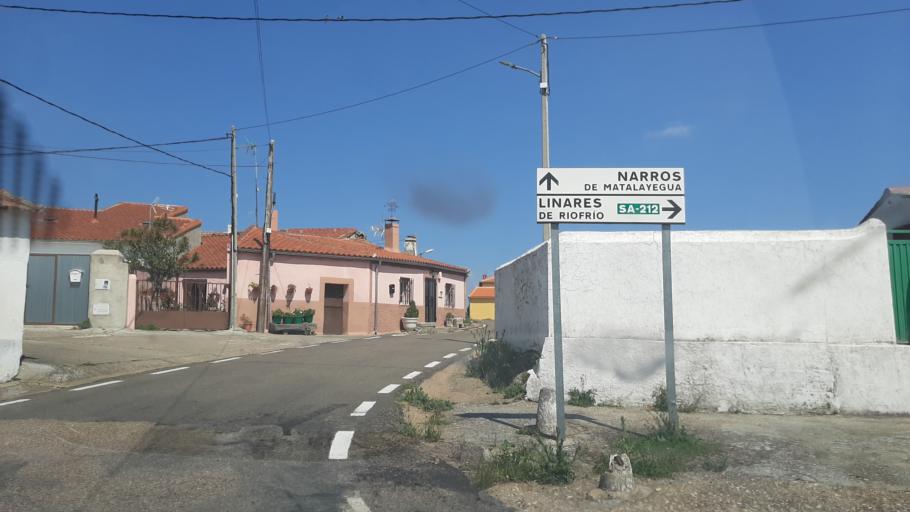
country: ES
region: Castille and Leon
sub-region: Provincia de Salamanca
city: Tejeda y Segoyuela
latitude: 40.6320
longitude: -6.0222
